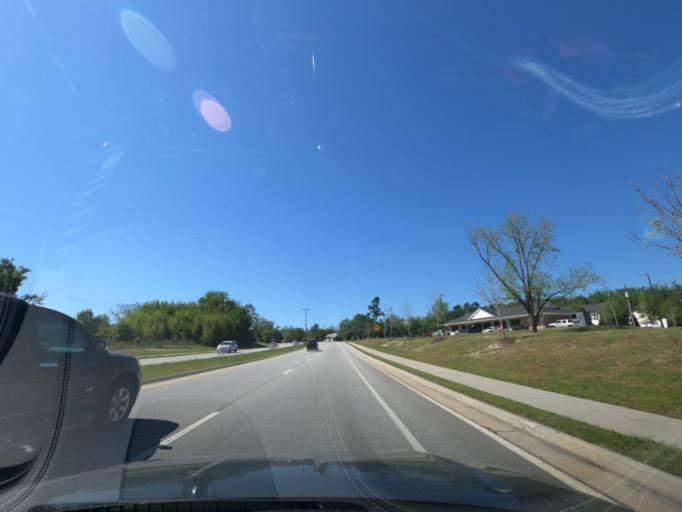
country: US
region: Georgia
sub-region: Columbia County
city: Martinez
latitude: 33.4672
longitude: -82.0958
